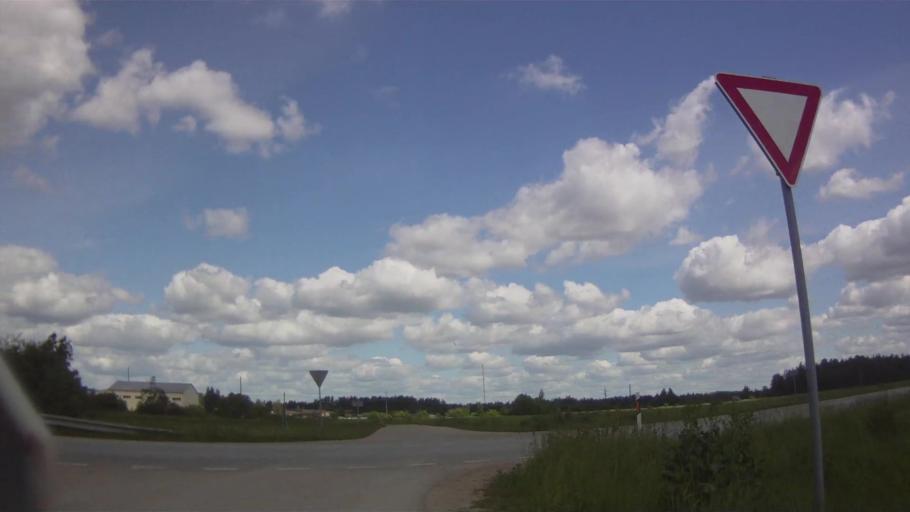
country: LV
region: Livani
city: Livani
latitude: 56.5335
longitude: 26.2446
